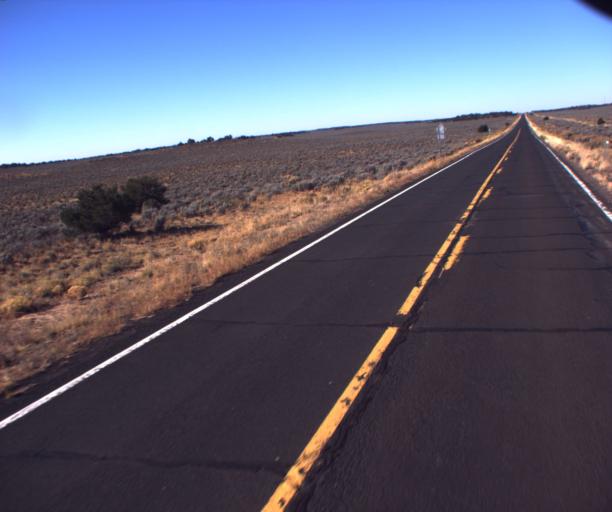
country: US
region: Arizona
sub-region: Navajo County
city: First Mesa
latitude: 35.7506
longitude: -110.0417
